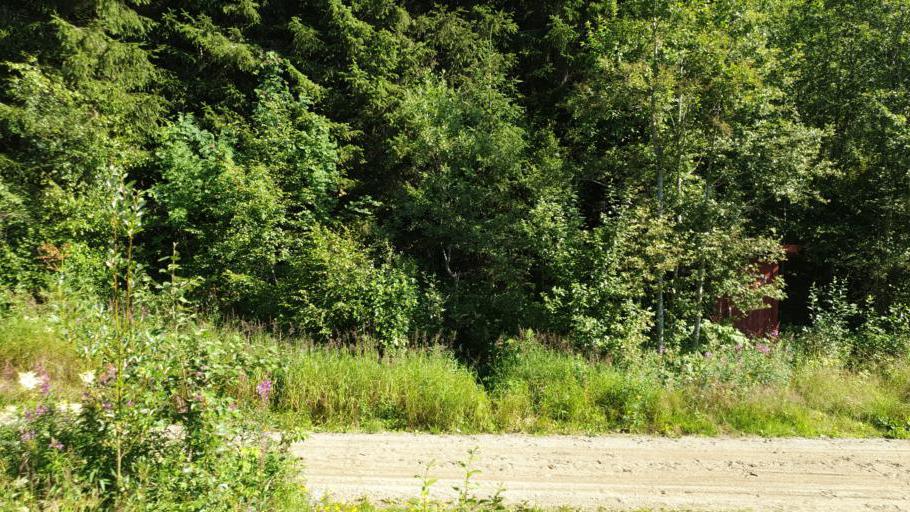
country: NO
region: Sor-Trondelag
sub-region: Orkdal
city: Orkanger
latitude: 63.1890
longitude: 9.7790
